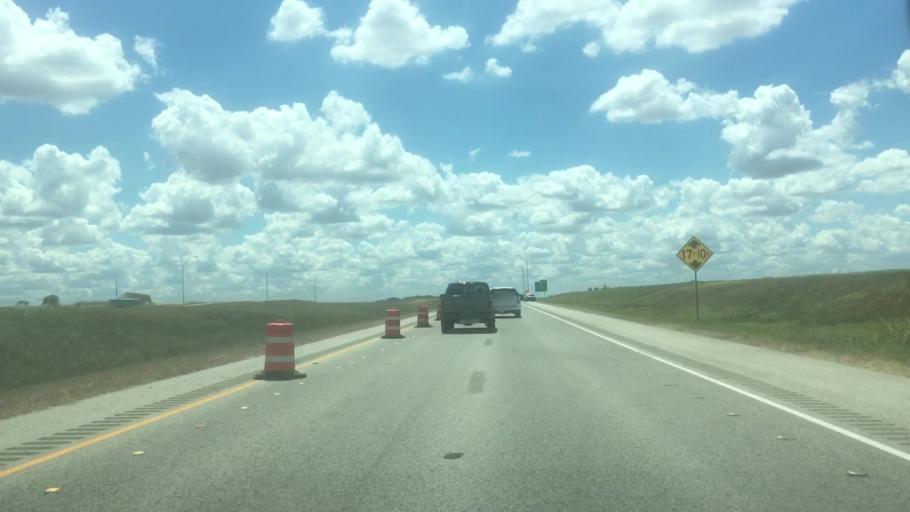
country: US
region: Texas
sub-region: Caldwell County
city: Martindale
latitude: 29.7920
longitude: -97.7836
